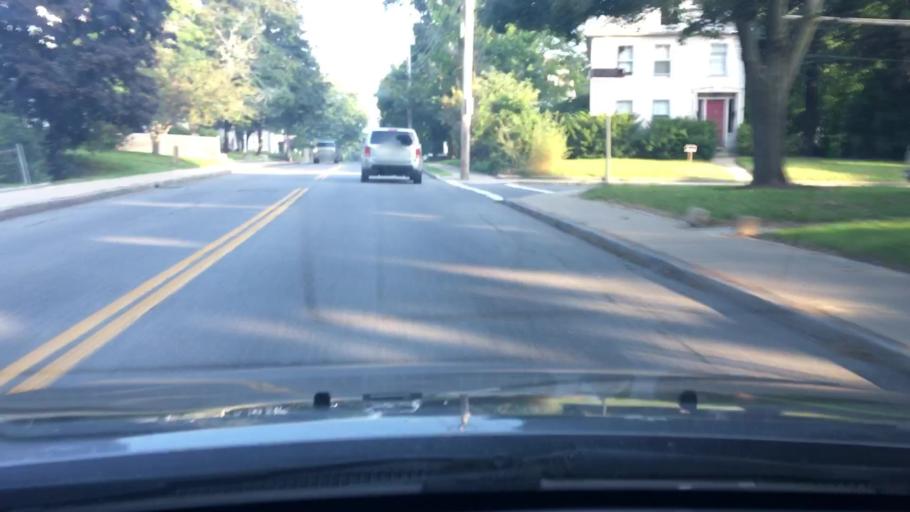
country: US
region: Massachusetts
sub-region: Worcester County
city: Westborough
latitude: 42.2685
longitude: -71.6175
